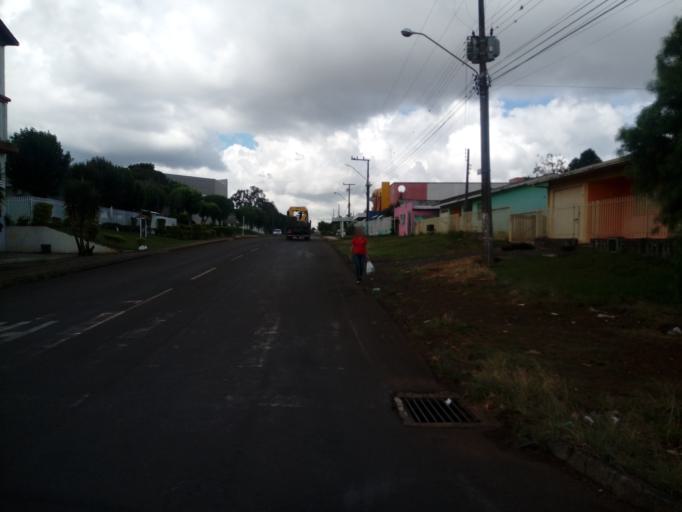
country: BR
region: Santa Catarina
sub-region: Chapeco
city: Chapeco
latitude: -27.0827
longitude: -52.6080
